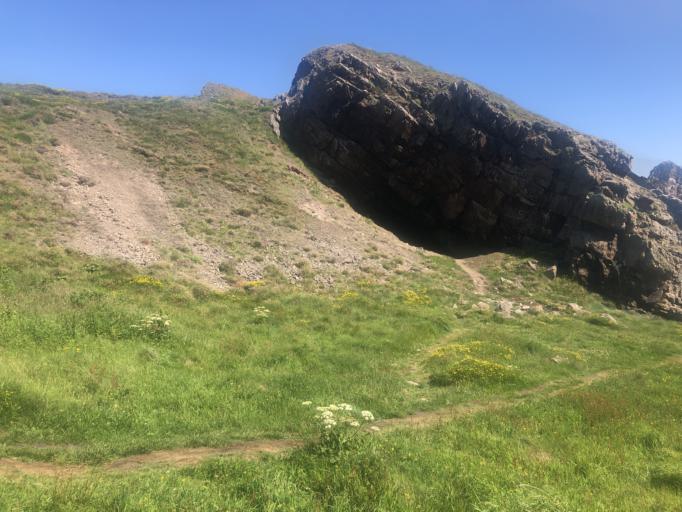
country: GB
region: Scotland
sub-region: Moray
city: Portknockie
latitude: 57.7056
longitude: -2.8536
